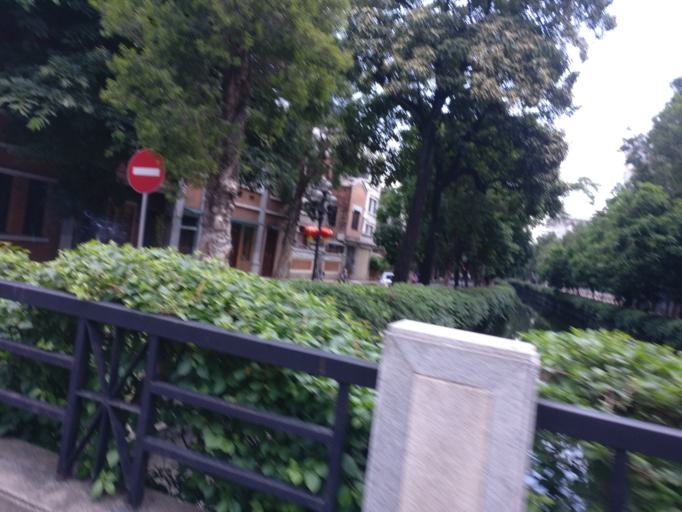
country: CN
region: Guangdong
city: Guangzhou
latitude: 23.1213
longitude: 113.2887
